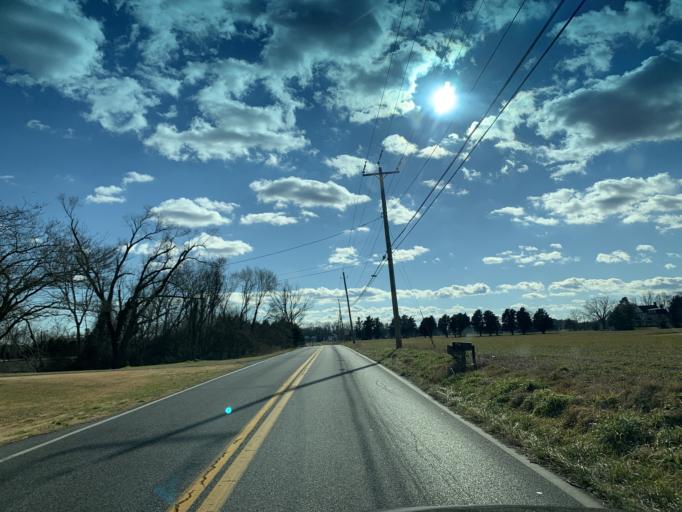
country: US
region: Maryland
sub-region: Worcester County
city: Berlin
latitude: 38.3389
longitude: -75.2200
